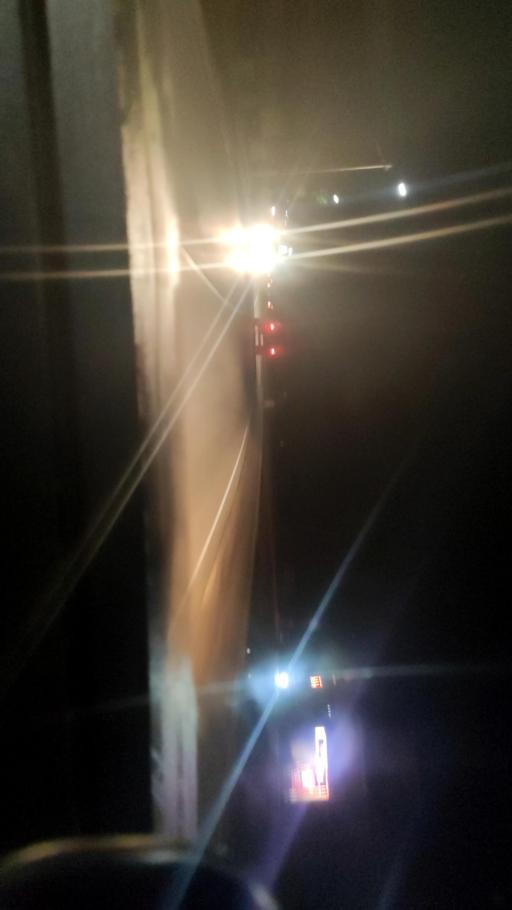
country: RU
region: Voronezj
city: Novaya Usman'
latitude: 51.6178
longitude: 39.3958
